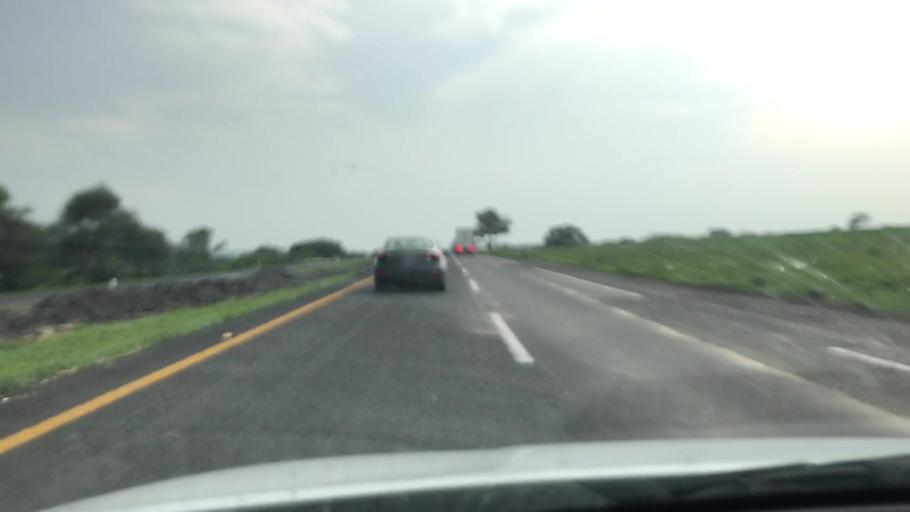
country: MX
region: Jalisco
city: La Barca
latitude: 20.3391
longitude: -102.6046
